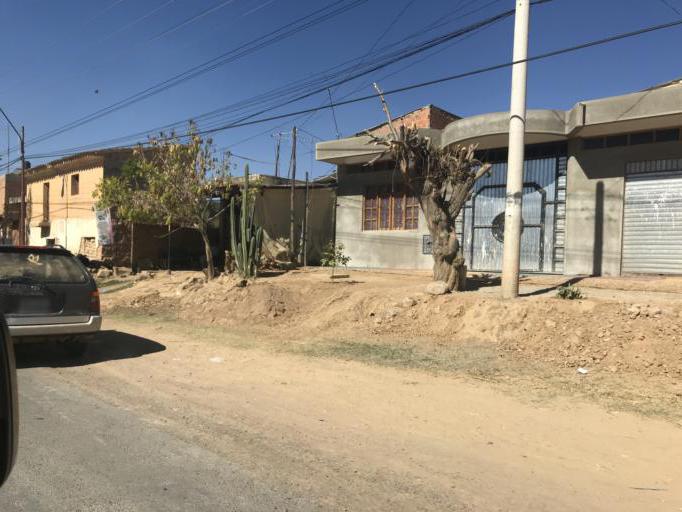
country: BO
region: Cochabamba
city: Cliza
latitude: -17.5760
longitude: -65.9052
